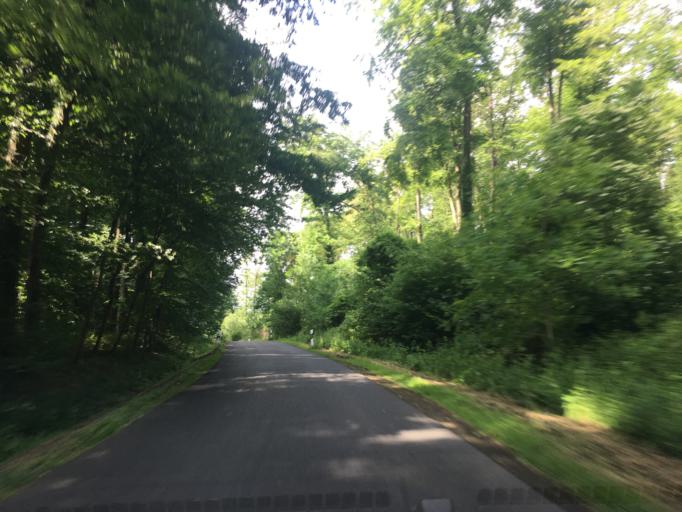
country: DE
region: North Rhine-Westphalia
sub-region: Regierungsbezirk Munster
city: Muenster
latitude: 52.0064
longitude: 7.5723
